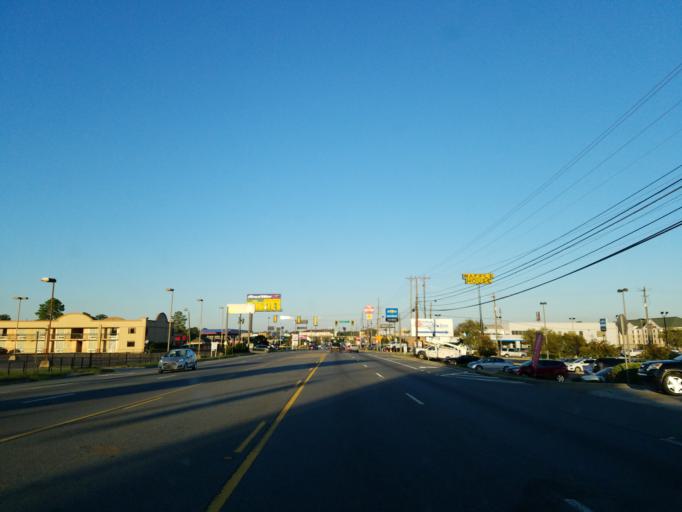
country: US
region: Georgia
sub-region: Tift County
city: Tifton
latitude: 31.4477
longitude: -83.5379
